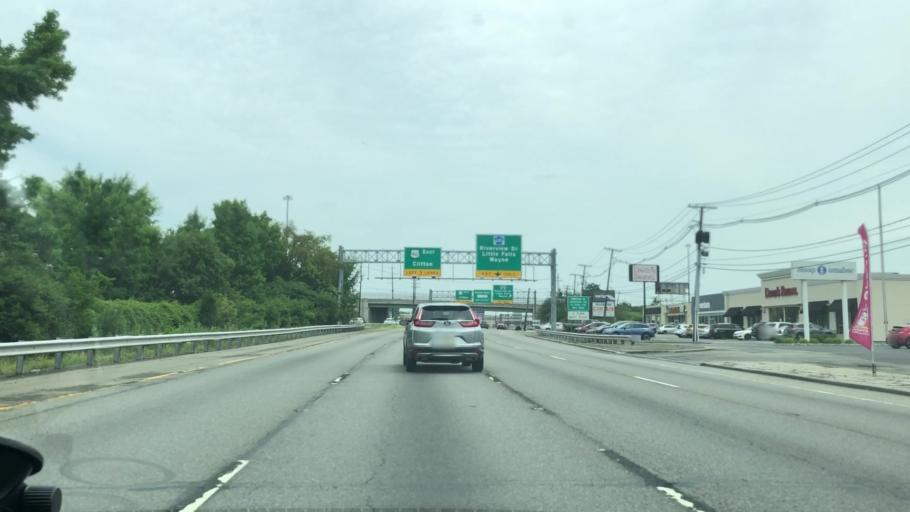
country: US
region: New Jersey
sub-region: Passaic County
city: Singac
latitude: 40.8949
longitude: -74.2393
